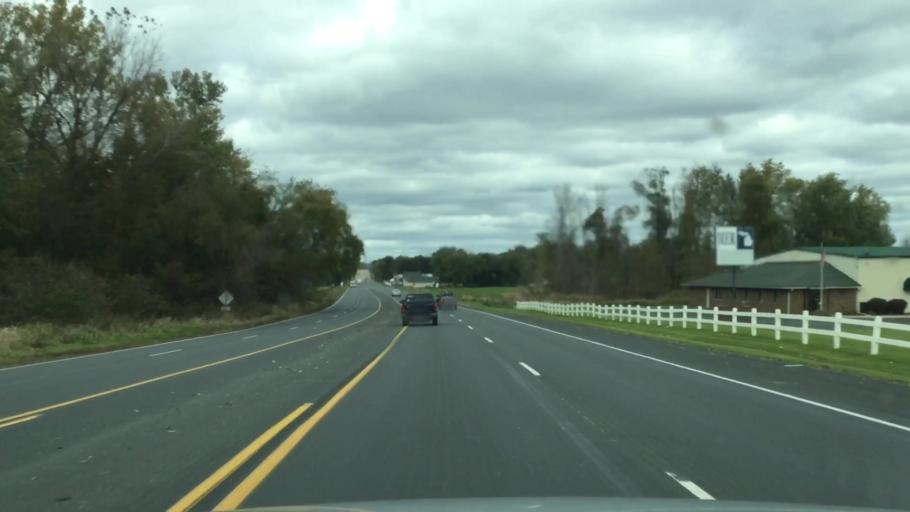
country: US
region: Michigan
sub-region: Kalamazoo County
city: Eastwood
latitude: 42.2729
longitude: -85.5308
